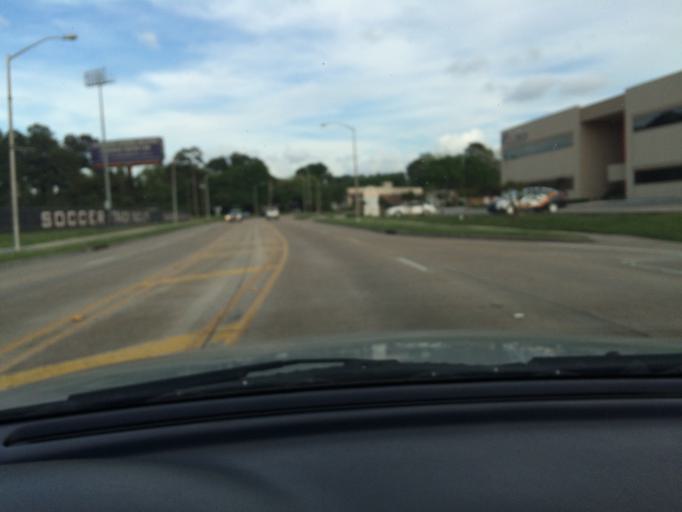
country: US
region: Louisiana
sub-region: Lafayette Parish
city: Lafayette
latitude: 30.2118
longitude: -92.0444
